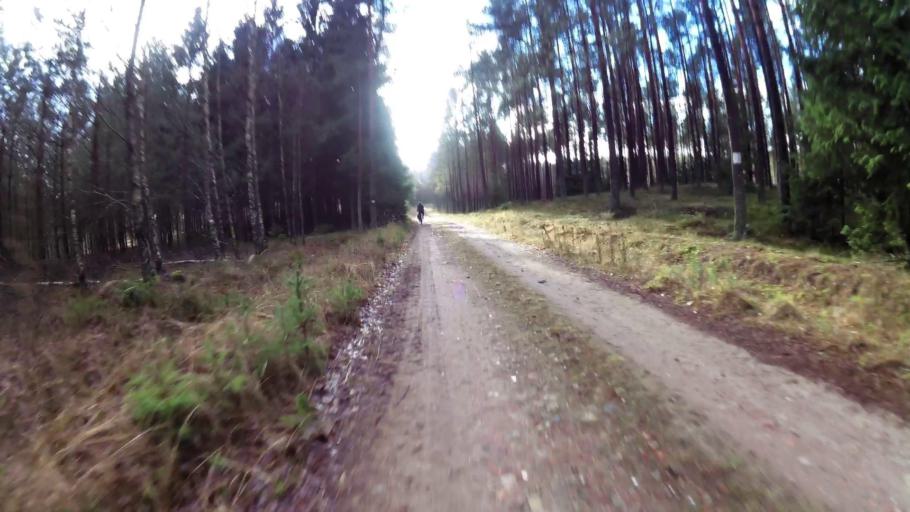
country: PL
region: West Pomeranian Voivodeship
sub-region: Powiat koszalinski
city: Sianow
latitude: 54.0862
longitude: 16.2921
